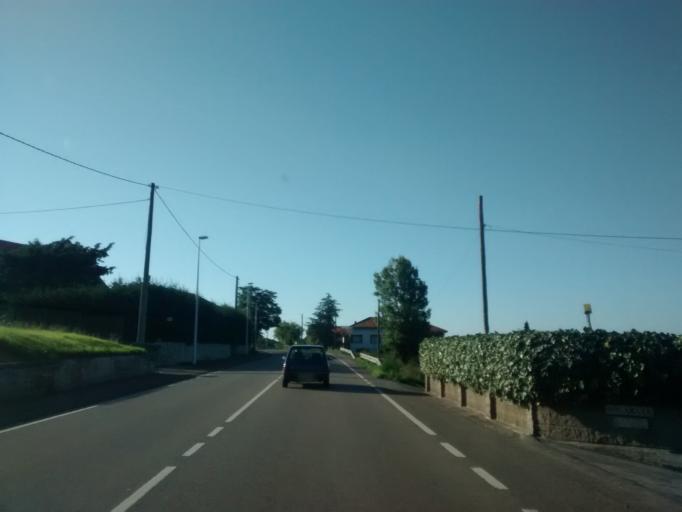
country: ES
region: Cantabria
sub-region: Provincia de Cantabria
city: Santander
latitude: 43.4267
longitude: -3.7702
